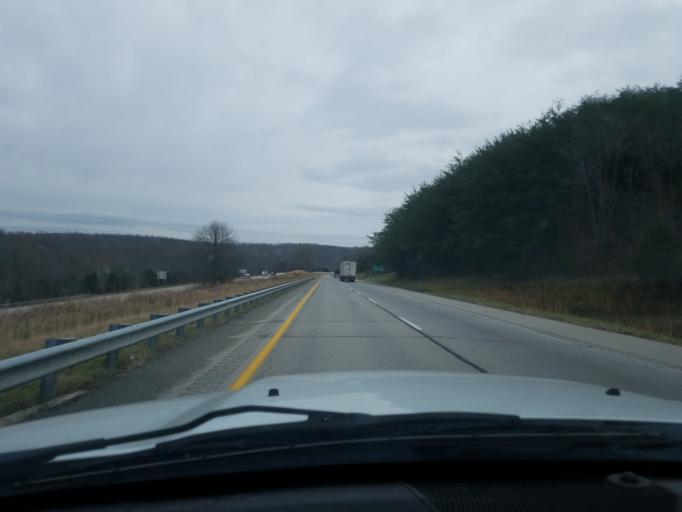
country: US
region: Indiana
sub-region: Crawford County
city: English
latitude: 38.2468
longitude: -86.3455
